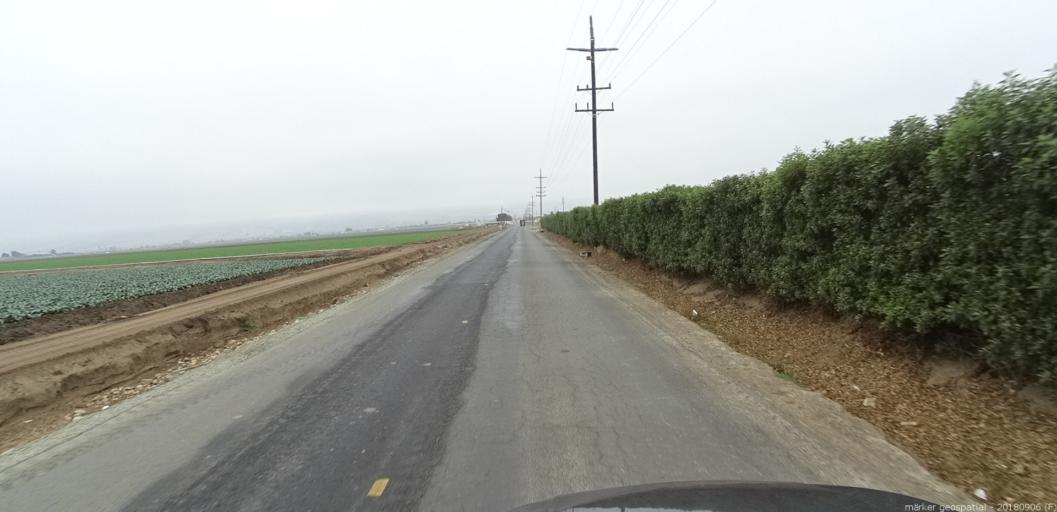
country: US
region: California
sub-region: Monterey County
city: Chualar
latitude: 36.6214
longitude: -121.5535
